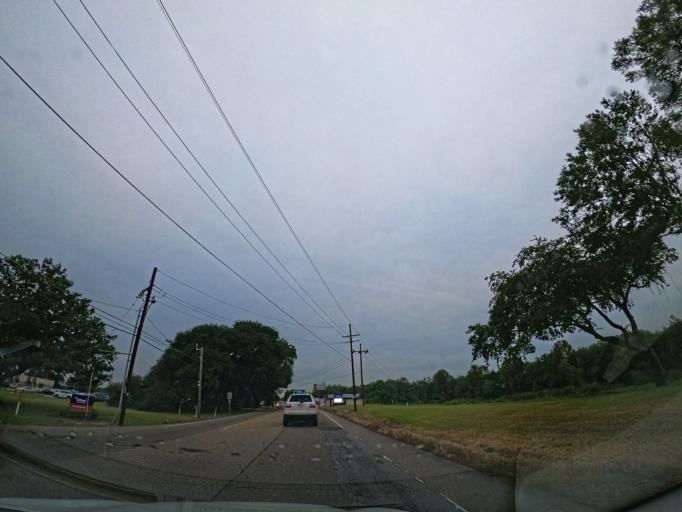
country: US
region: Louisiana
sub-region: Lafourche Parish
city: Mathews
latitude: 29.7034
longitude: -90.5641
